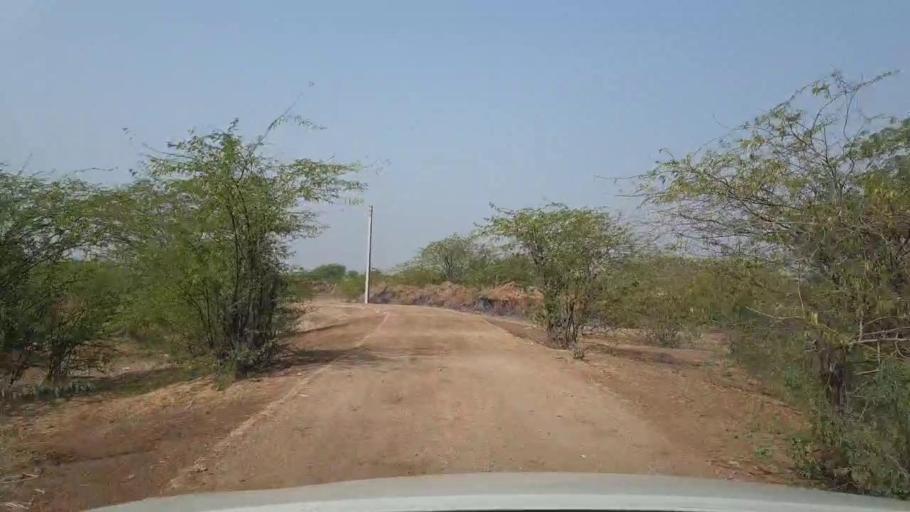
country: PK
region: Sindh
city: Chor
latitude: 25.4750
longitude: 69.7068
